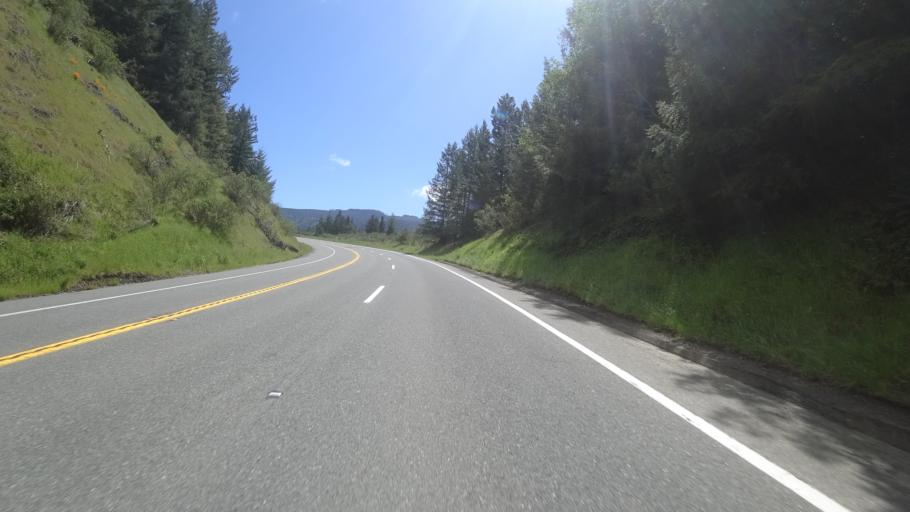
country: US
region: California
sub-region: Humboldt County
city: Blue Lake
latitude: 40.9277
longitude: -123.9050
